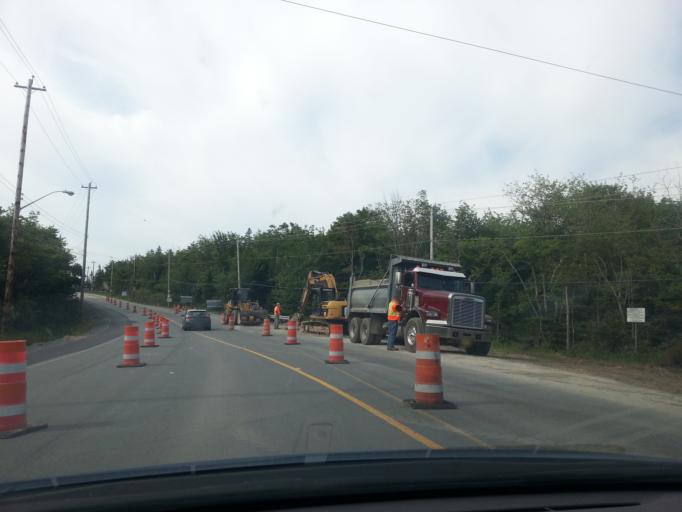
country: CA
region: Nova Scotia
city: Halifax
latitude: 44.6311
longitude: -63.6635
